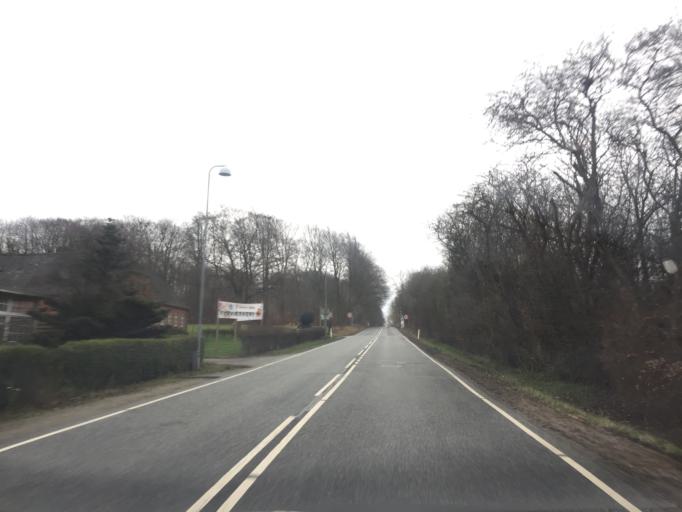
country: DK
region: South Denmark
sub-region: Svendborg Kommune
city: Thuro By
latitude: 55.1533
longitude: 10.6730
